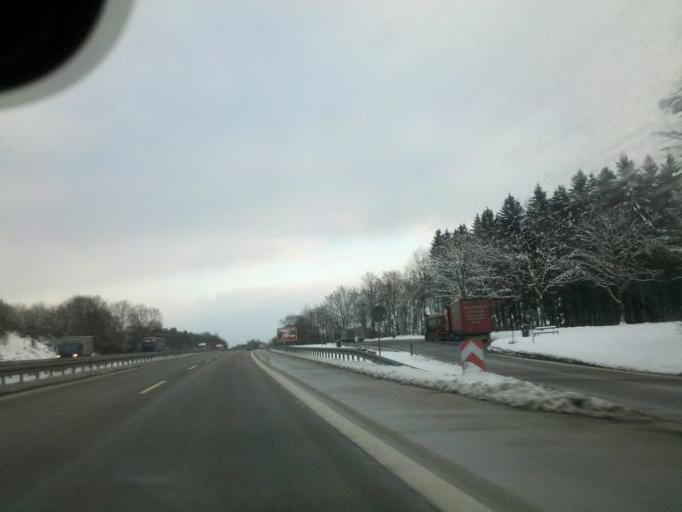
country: DE
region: North Rhine-Westphalia
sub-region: Regierungsbezirk Arnsberg
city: Drolshagen
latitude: 51.0462
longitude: 7.7958
